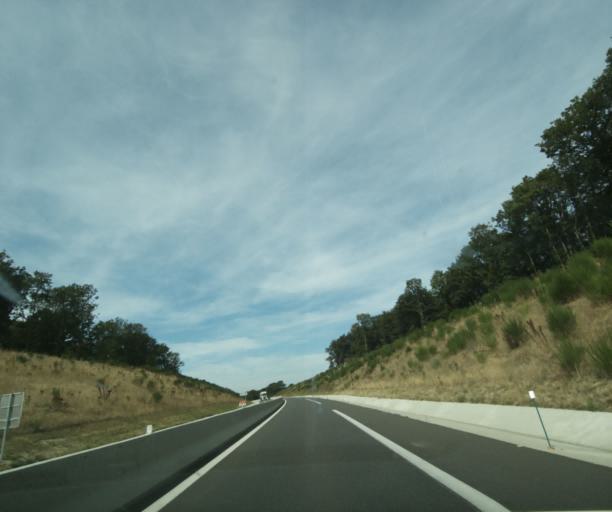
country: FR
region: Auvergne
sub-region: Departement de l'Allier
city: Vendat
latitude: 46.1344
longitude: 3.3597
